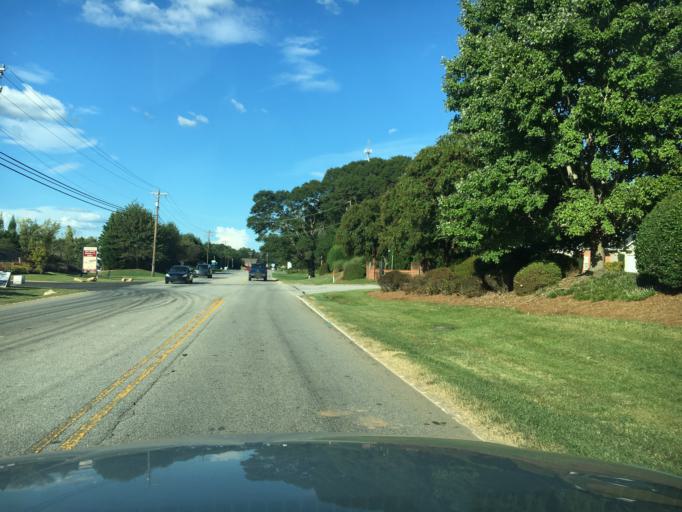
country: US
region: South Carolina
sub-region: Greenville County
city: Simpsonville
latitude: 34.7440
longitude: -82.2307
